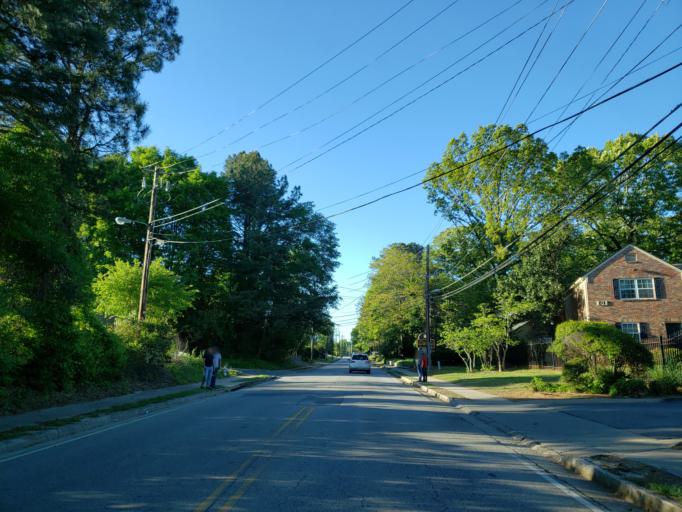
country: US
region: Georgia
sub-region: Cobb County
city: Fair Oaks
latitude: 33.9046
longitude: -84.5400
